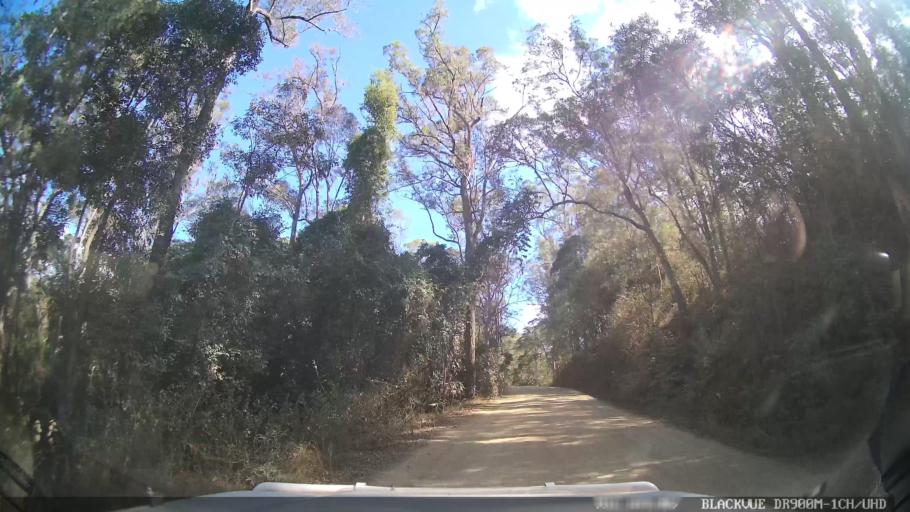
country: AU
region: Queensland
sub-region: Moreton Bay
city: Woodford
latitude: -26.6689
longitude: 152.6360
